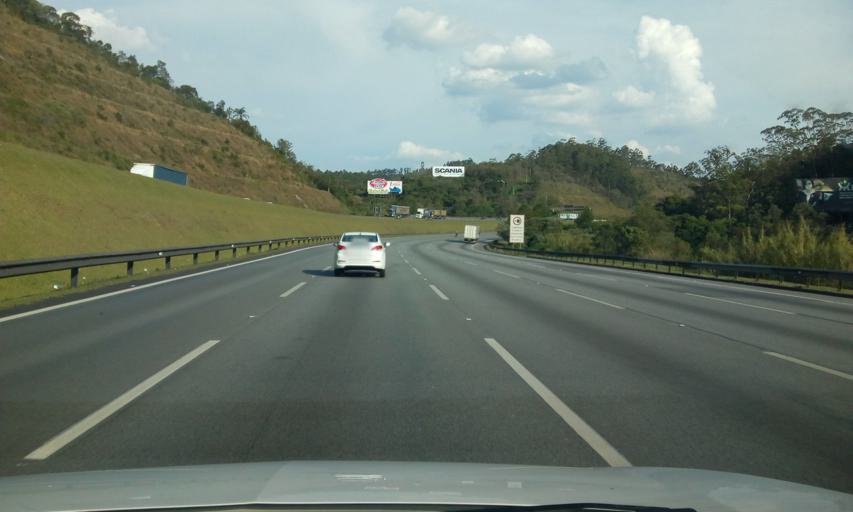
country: BR
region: Sao Paulo
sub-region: Varzea Paulista
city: Varzea Paulista
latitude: -23.2756
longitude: -46.8511
